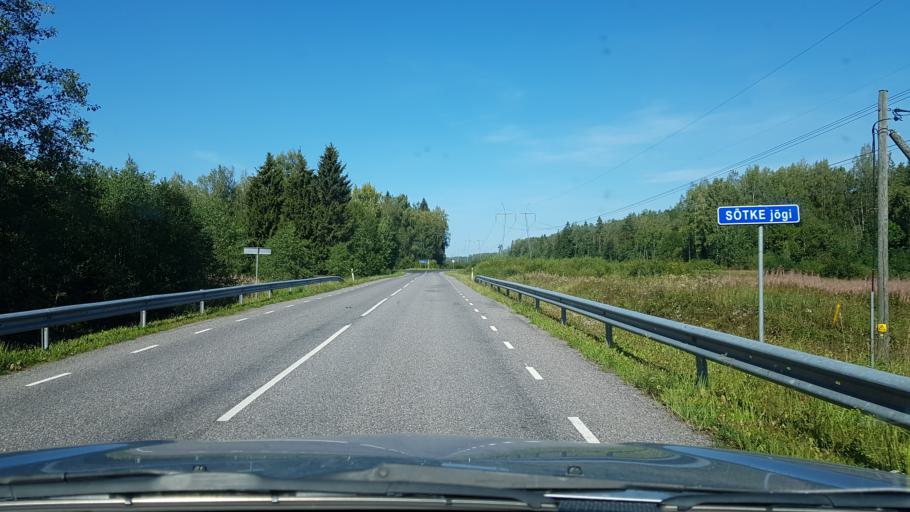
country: EE
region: Ida-Virumaa
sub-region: Sillamaee linn
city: Sillamae
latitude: 59.3508
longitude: 27.7456
